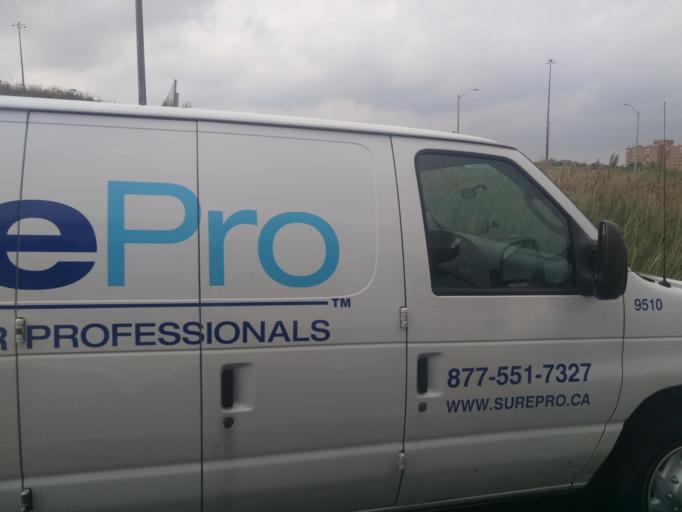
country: CA
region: Ontario
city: Mississauga
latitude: 43.5228
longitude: -79.6470
